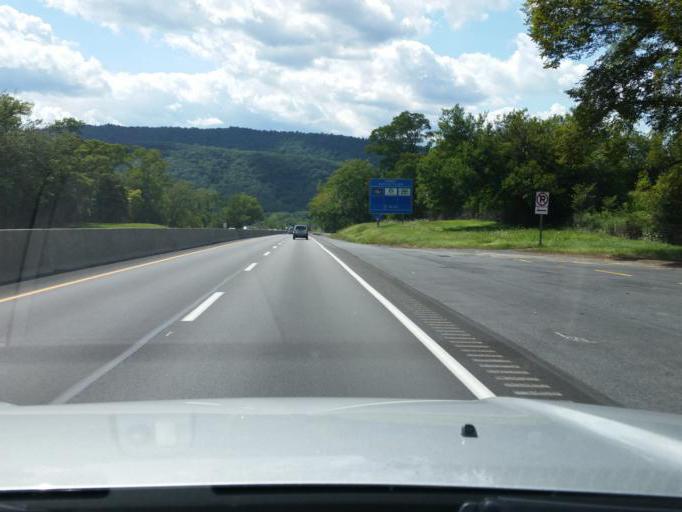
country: US
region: Pennsylvania
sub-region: Bedford County
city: Bedford
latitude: 40.0116
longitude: -78.4552
